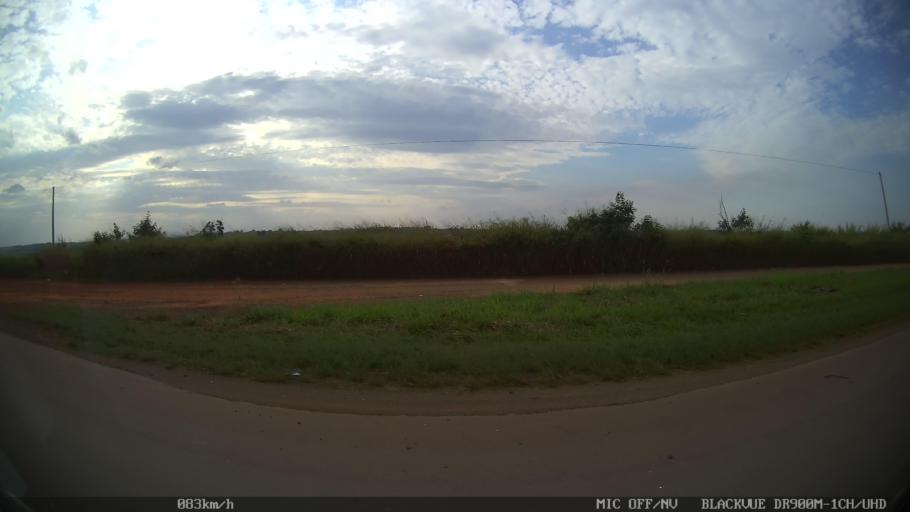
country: BR
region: Sao Paulo
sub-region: Cosmopolis
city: Cosmopolis
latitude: -22.6263
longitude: -47.2615
